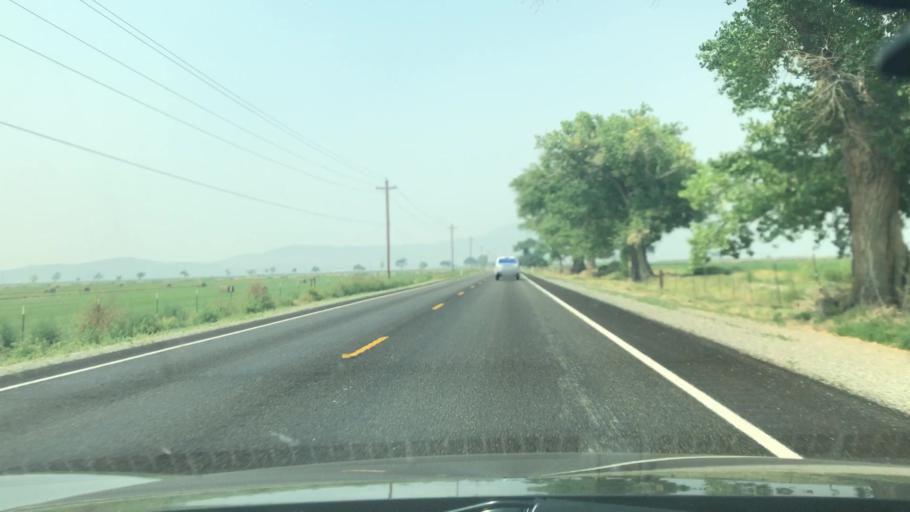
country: US
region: Nevada
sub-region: Lyon County
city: Yerington
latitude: 39.1211
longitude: -119.1810
